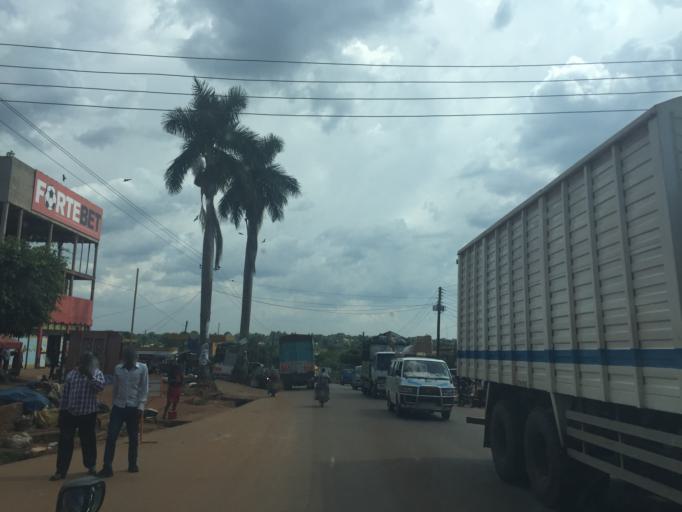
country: UG
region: Central Region
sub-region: Luwero District
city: Wobulenzi
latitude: 0.7173
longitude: 32.5283
